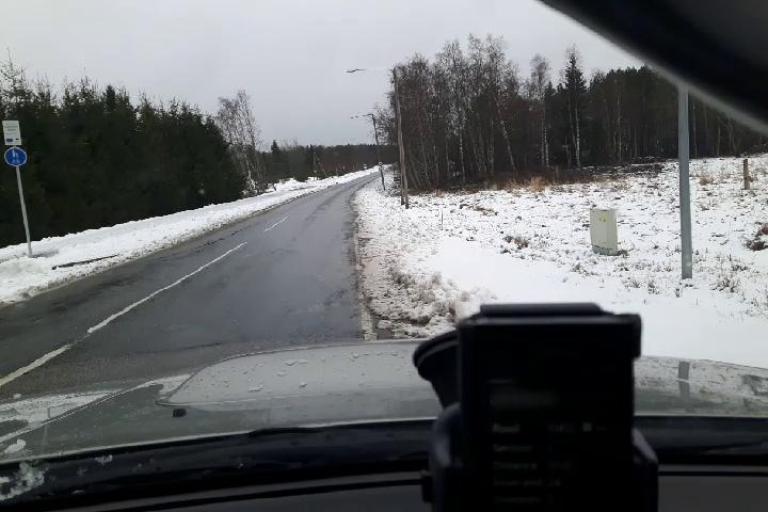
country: EE
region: Harju
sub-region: Harku vald
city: Tabasalu
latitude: 59.4369
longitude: 24.4985
